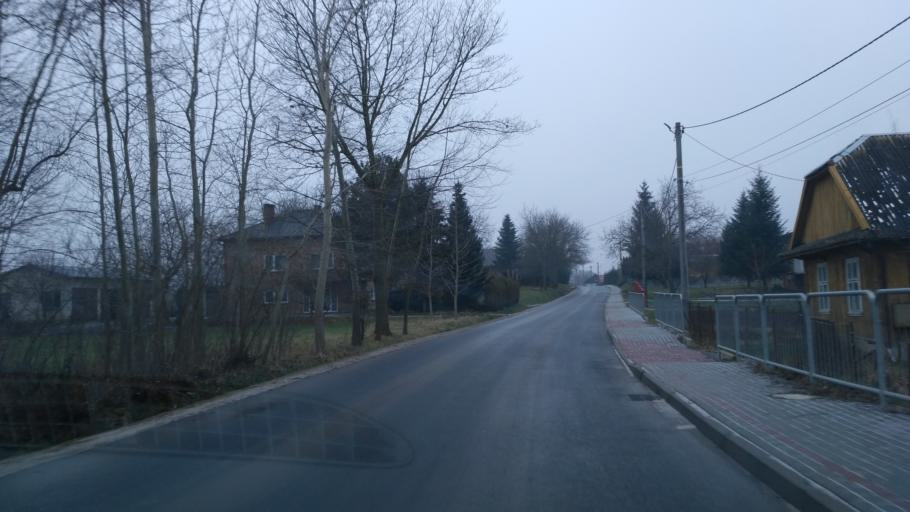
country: PL
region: Subcarpathian Voivodeship
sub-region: Powiat przeworski
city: Kanczuga
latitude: 50.0163
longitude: 22.4082
